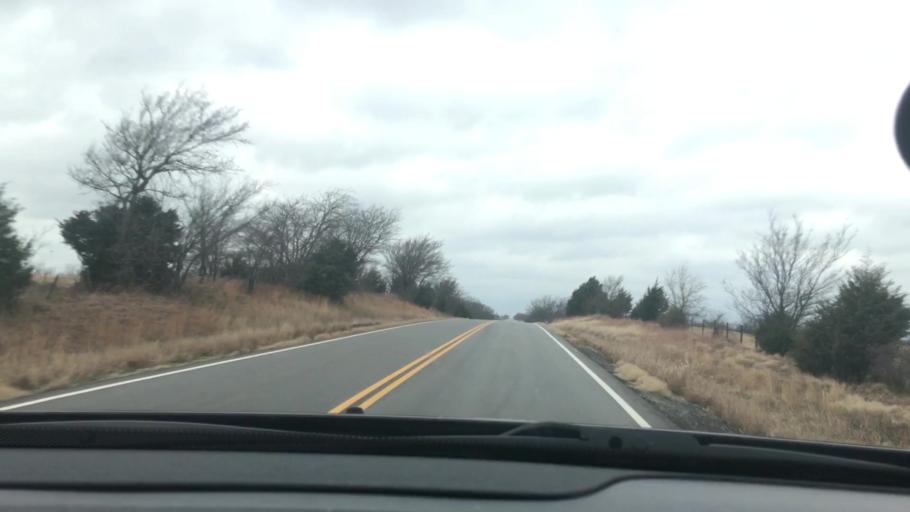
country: US
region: Oklahoma
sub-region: Atoka County
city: Atoka
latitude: 34.3750
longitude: -96.2071
